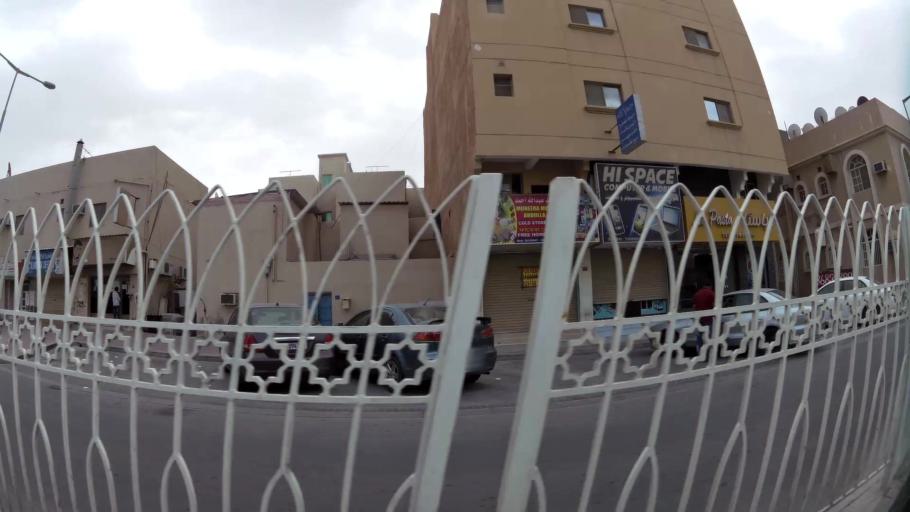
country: BH
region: Northern
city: Ar Rifa'
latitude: 26.1275
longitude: 50.5440
